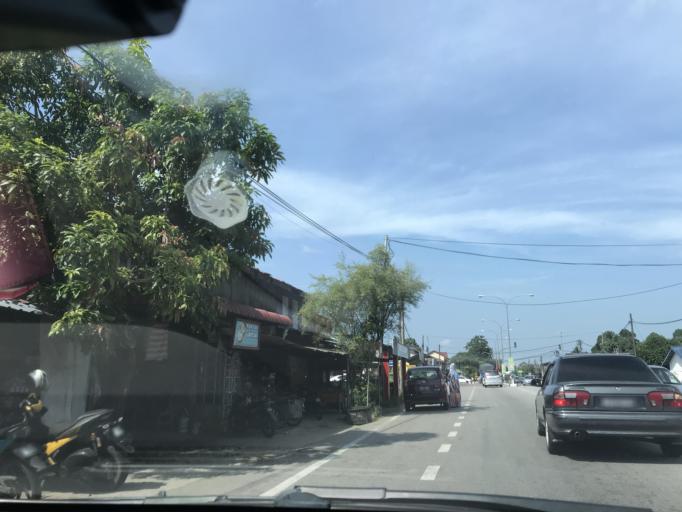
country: MY
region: Kelantan
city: Tumpat
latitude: 6.1536
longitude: 102.1574
